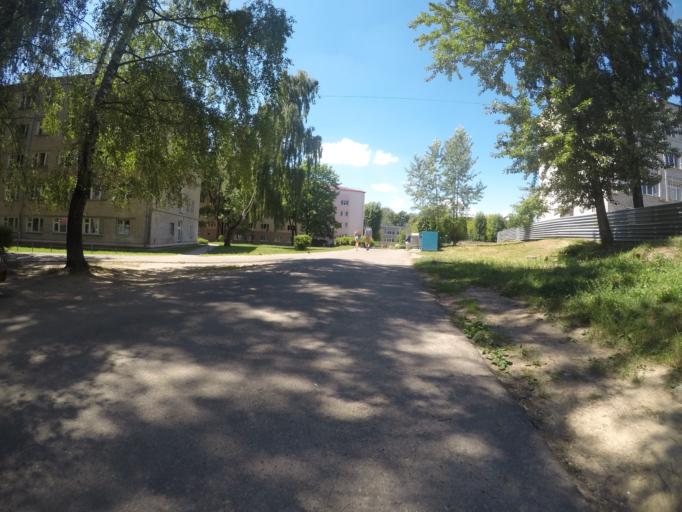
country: BY
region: Grodnenskaya
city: Hrodna
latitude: 53.6949
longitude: 23.8270
